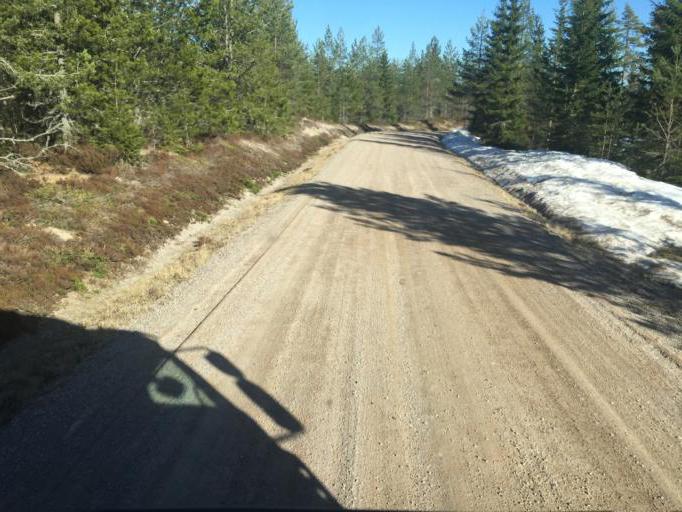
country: SE
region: Vaermland
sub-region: Filipstads Kommun
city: Lesjofors
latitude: 60.2508
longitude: 14.0842
